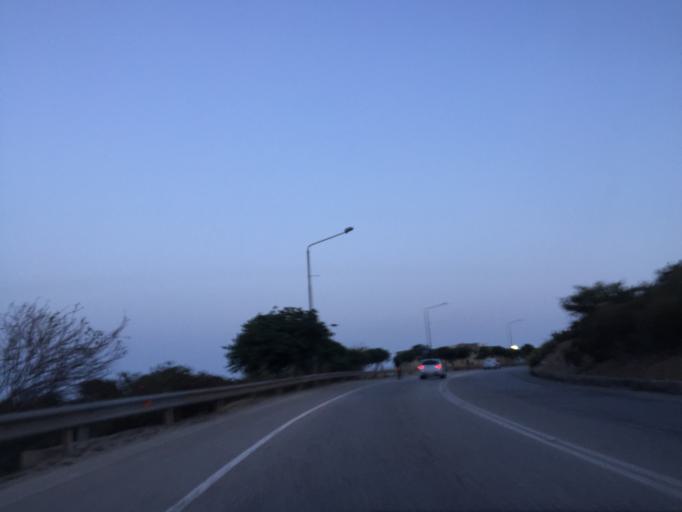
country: MT
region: Pembroke
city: Pembroke
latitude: 35.9270
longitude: 14.4718
